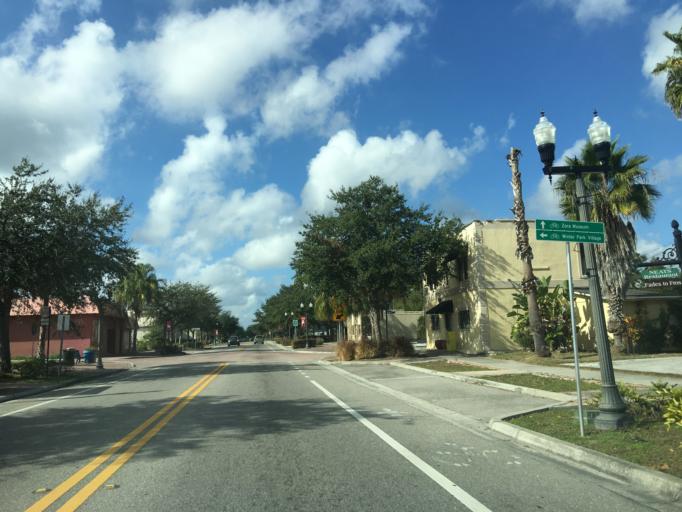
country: US
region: Florida
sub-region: Orange County
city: Eatonville
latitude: 28.6186
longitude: -81.3773
